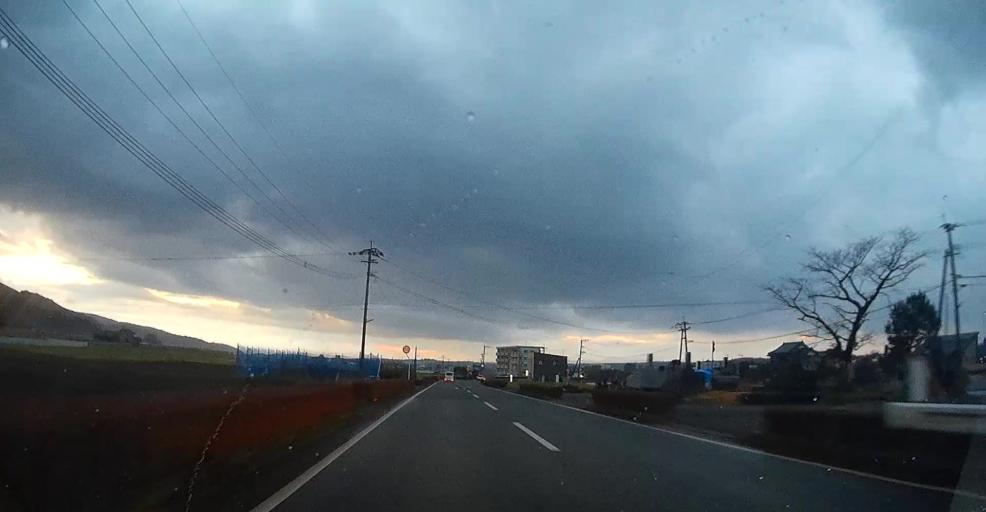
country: JP
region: Kumamoto
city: Ozu
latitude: 32.8391
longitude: 130.9132
